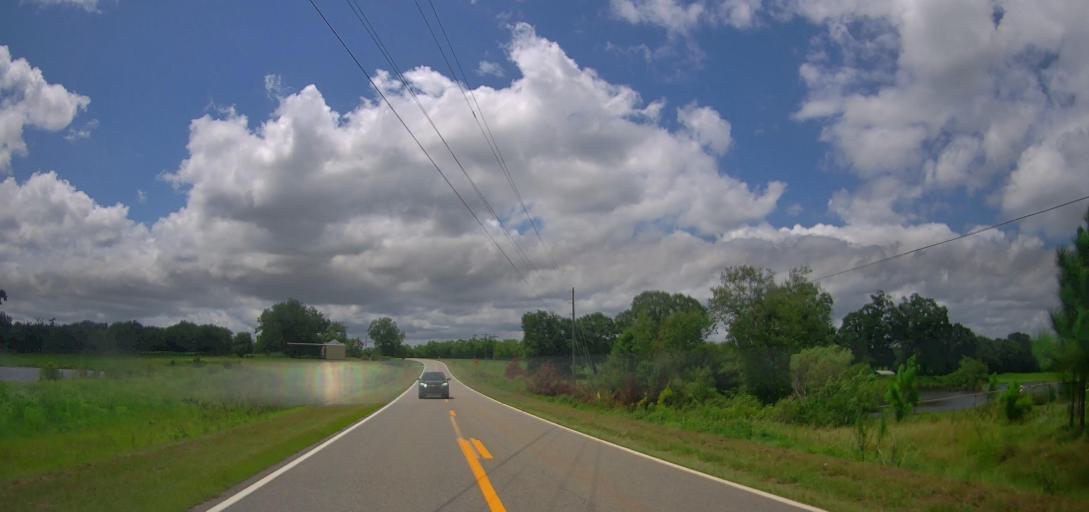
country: US
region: Georgia
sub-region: Irwin County
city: Ocilla
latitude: 31.6447
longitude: -83.2744
